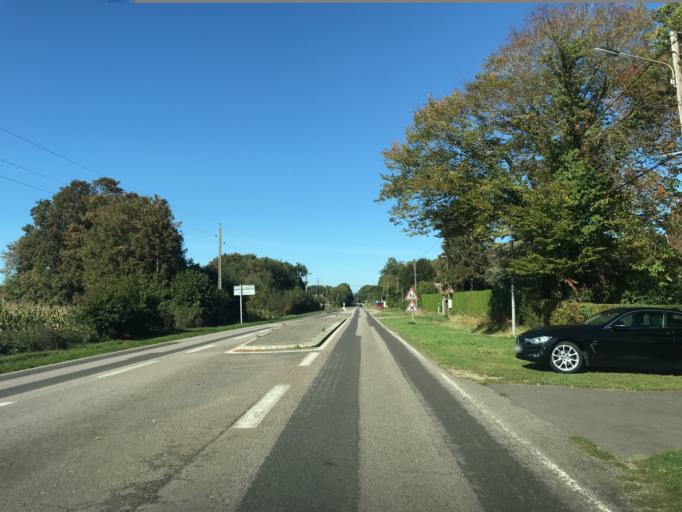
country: FR
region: Haute-Normandie
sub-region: Departement de l'Eure
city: Saint-Pierre-du-Vauvray
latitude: 49.2389
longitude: 1.2112
